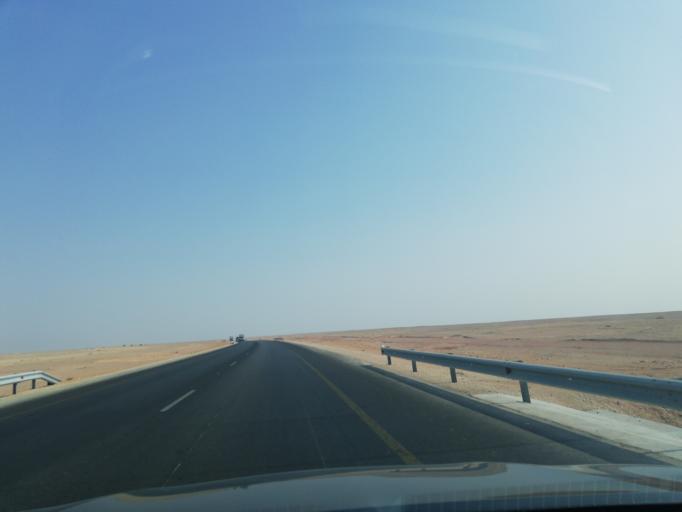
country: OM
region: Zufar
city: Salalah
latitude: 17.8120
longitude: 54.0001
